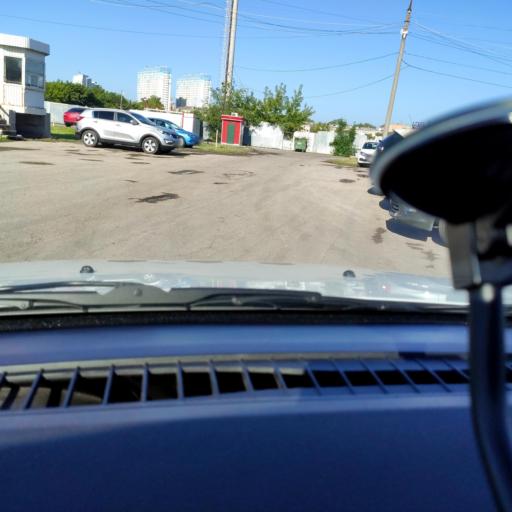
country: RU
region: Samara
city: Samara
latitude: 53.2107
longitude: 50.1991
